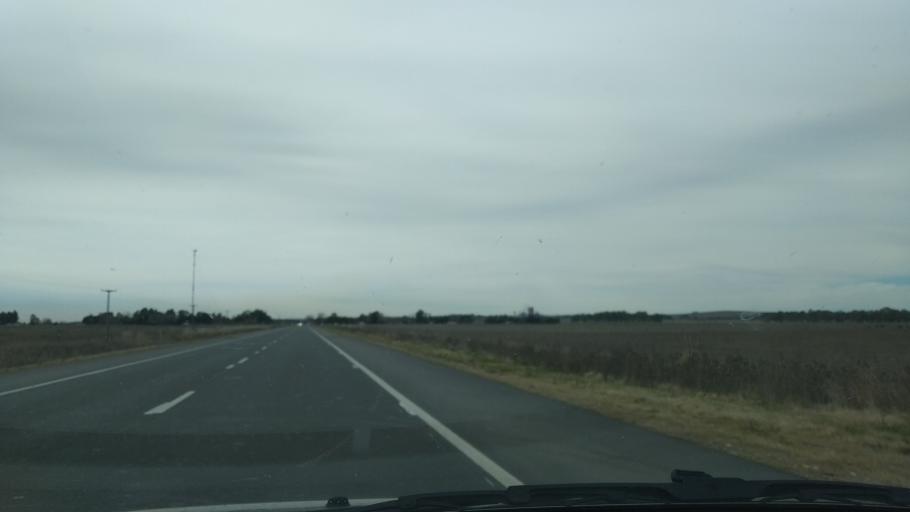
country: AR
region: Buenos Aires
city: Olavarria
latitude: -36.9935
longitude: -60.3251
